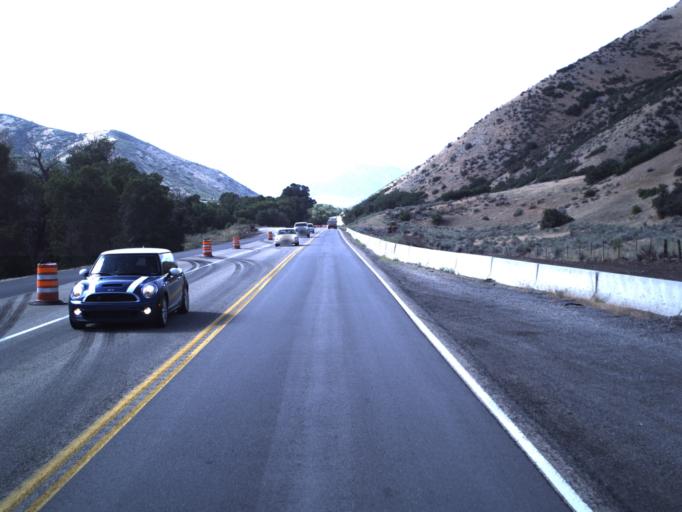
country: US
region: Utah
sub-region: Wasatch County
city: Heber
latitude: 40.4252
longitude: -111.3462
